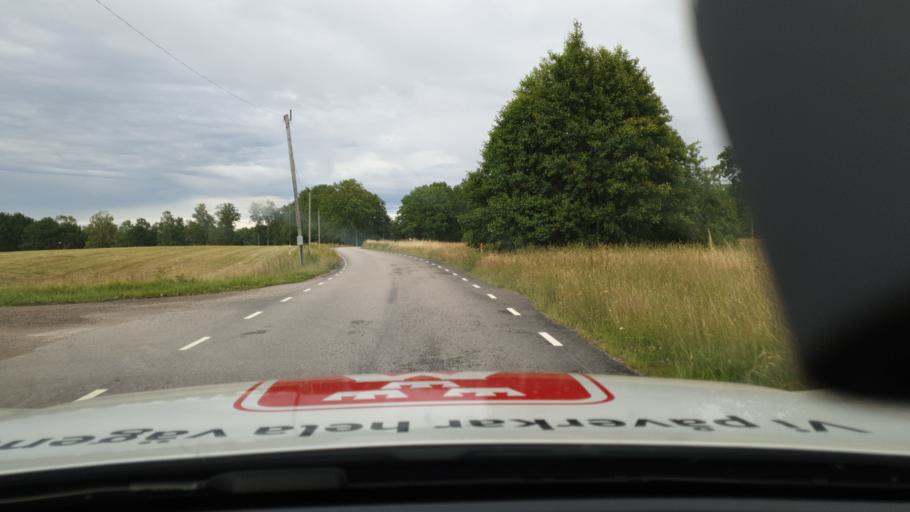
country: SE
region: Vaestra Goetaland
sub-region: Mariestads Kommun
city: Mariestad
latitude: 58.6153
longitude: 13.7277
